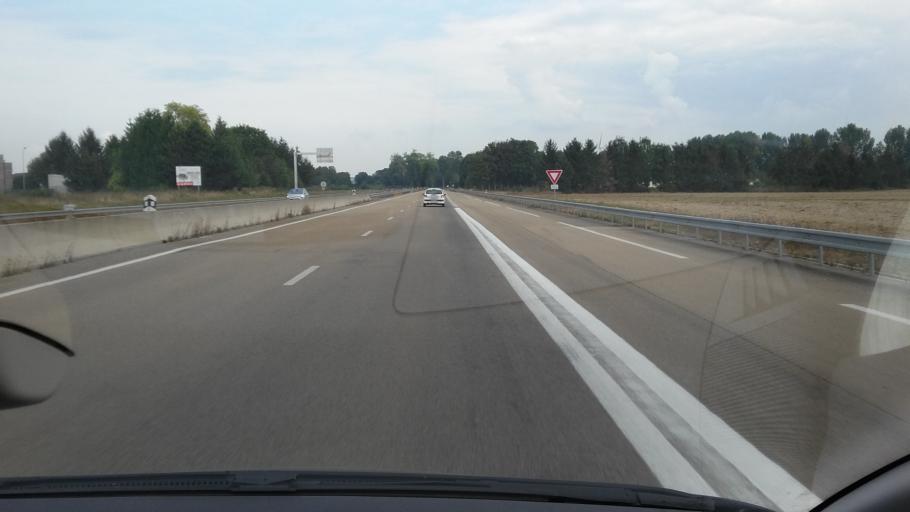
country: FR
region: Champagne-Ardenne
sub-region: Departement de la Marne
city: Fere-Champenoise
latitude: 48.7448
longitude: 3.9703
